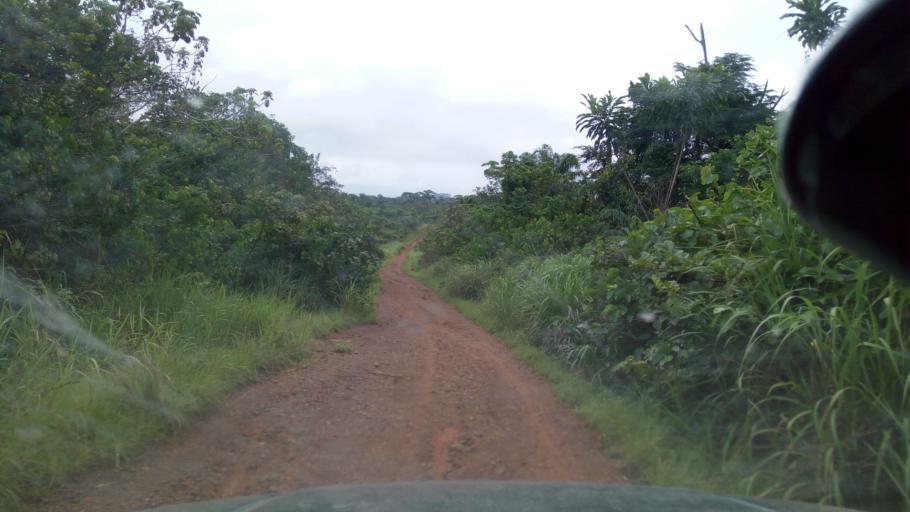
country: SL
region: Eastern Province
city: Gorahun
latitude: 7.5575
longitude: -11.1229
